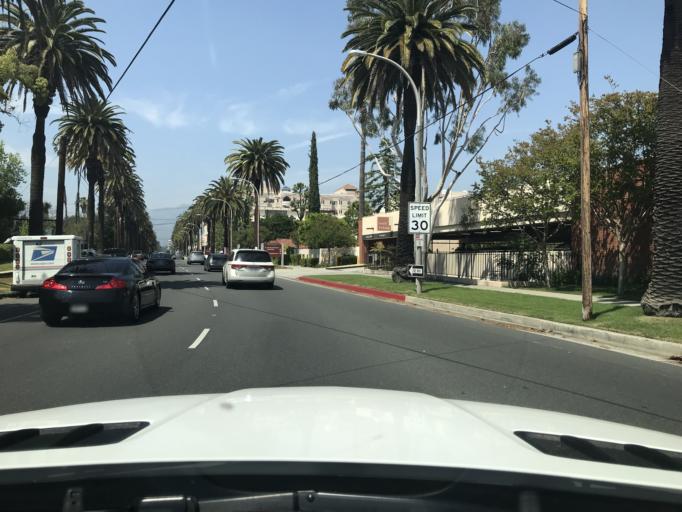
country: US
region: California
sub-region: Los Angeles County
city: South Pasadena
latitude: 34.1319
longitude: -118.1541
